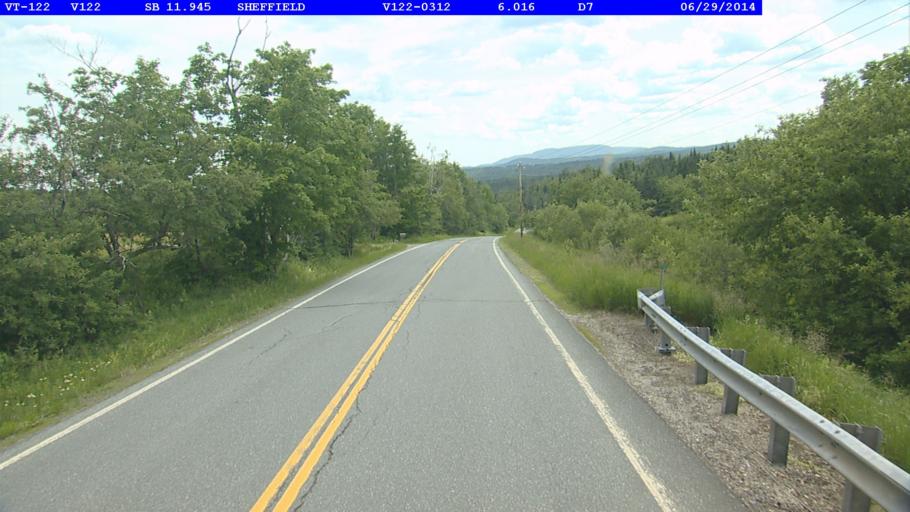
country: US
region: Vermont
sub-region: Caledonia County
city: Lyndonville
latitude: 44.6550
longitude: -72.1622
